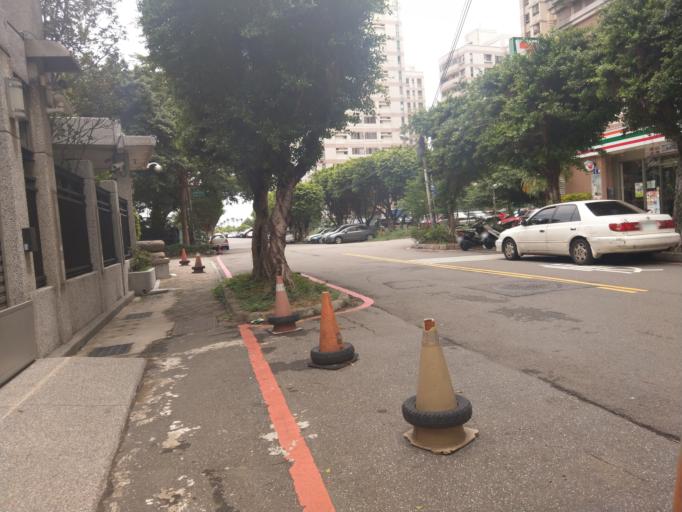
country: TW
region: Taiwan
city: Taoyuan City
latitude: 24.9457
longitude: 121.2484
